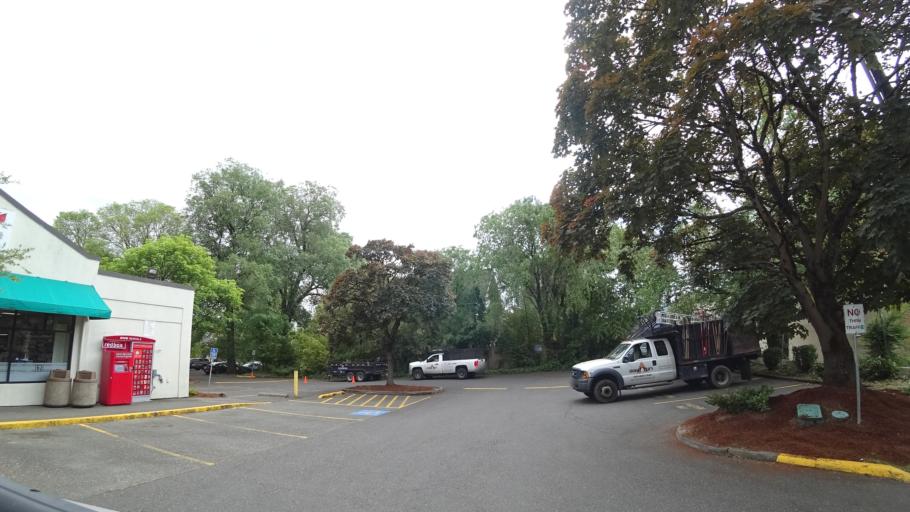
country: US
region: Oregon
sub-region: Multnomah County
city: Portland
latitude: 45.5121
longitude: -122.6459
